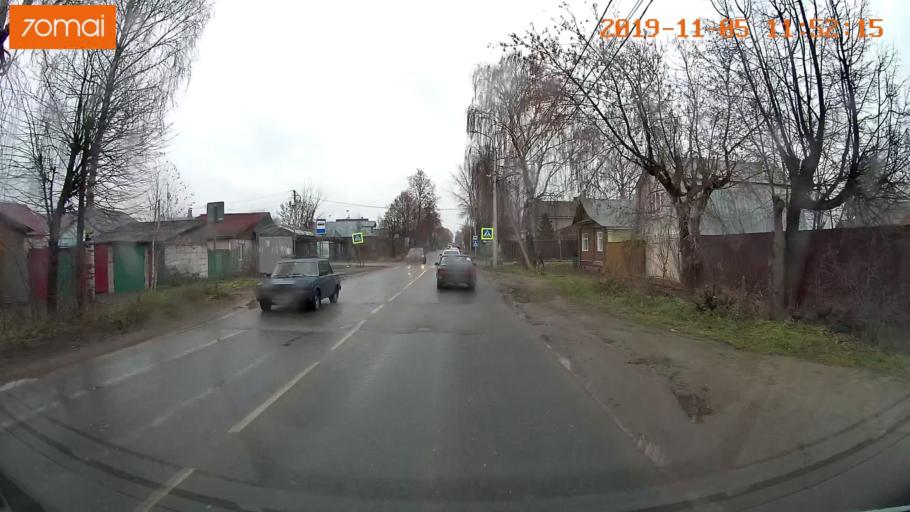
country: RU
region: Ivanovo
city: Bogorodskoye
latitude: 57.0008
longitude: 41.0293
